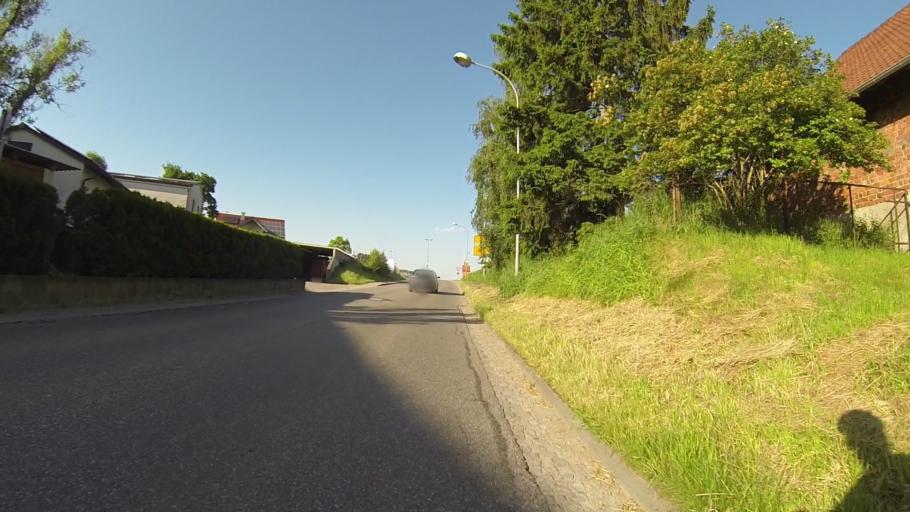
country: DE
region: Baden-Wuerttemberg
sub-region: Tuebingen Region
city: Mietingen
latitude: 48.1753
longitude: 9.8638
